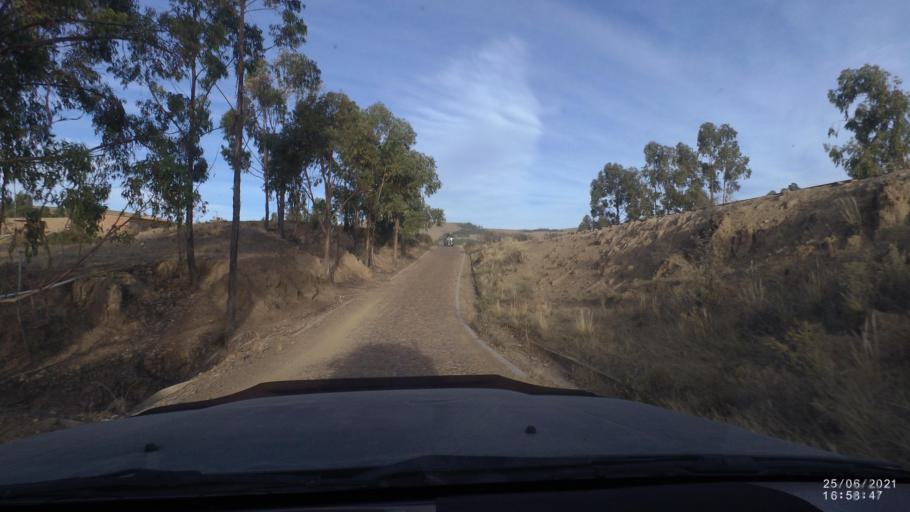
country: BO
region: Cochabamba
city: Arani
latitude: -17.8333
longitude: -65.7547
